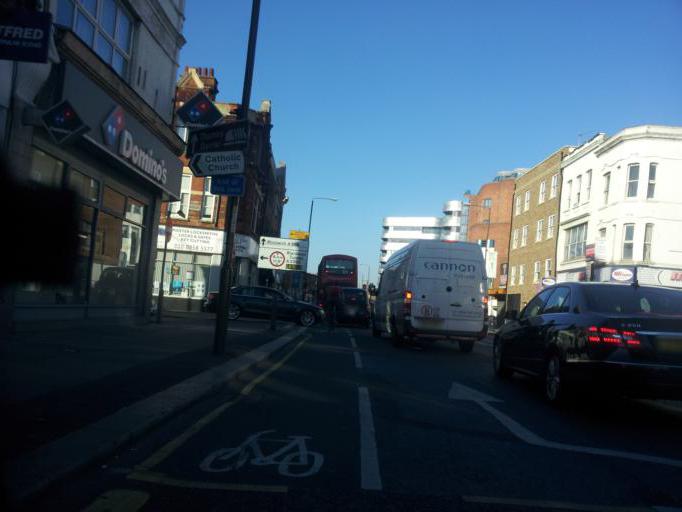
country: GB
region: England
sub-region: Greater London
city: Blackheath
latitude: 51.4855
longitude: 0.0062
